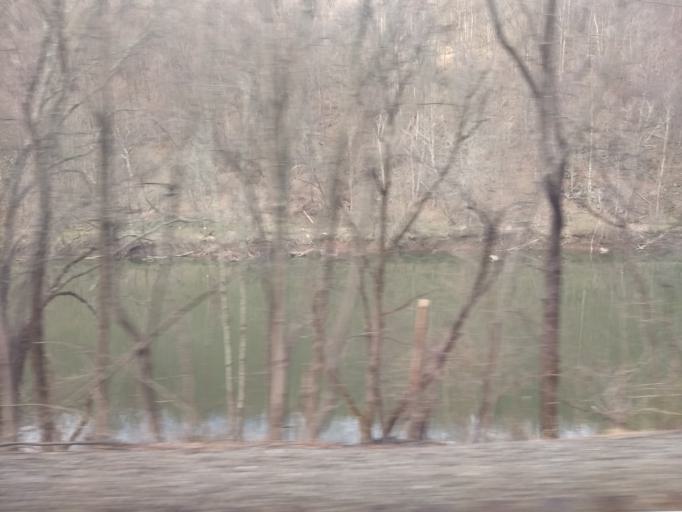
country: US
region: Pennsylvania
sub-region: Huntingdon County
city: Huntingdon
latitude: 40.5214
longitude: -78.0256
